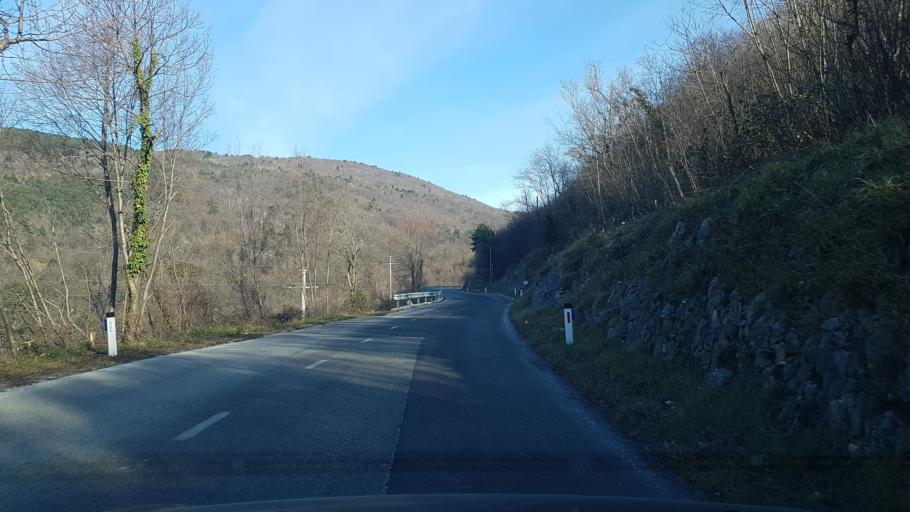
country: SI
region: Nova Gorica
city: Kromberk
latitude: 46.0071
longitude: 13.6910
